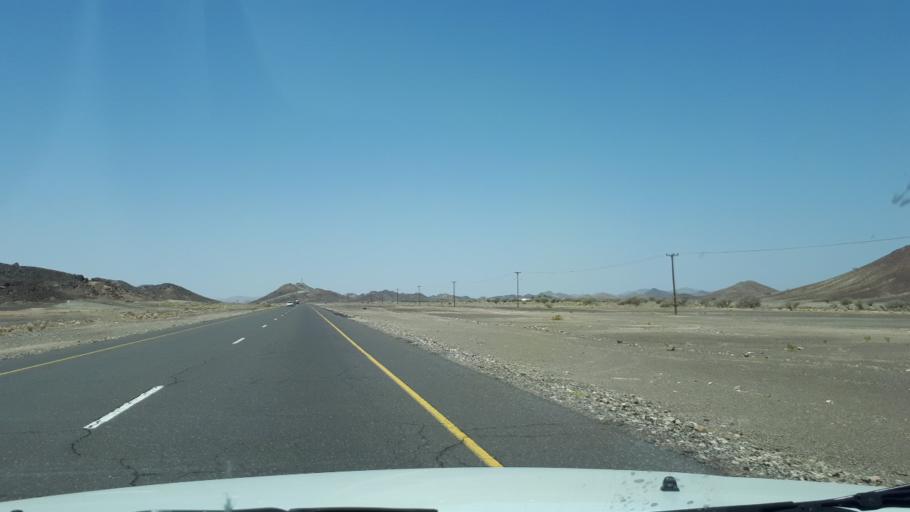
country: OM
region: Ash Sharqiyah
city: Ibra'
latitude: 22.6346
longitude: 58.4691
